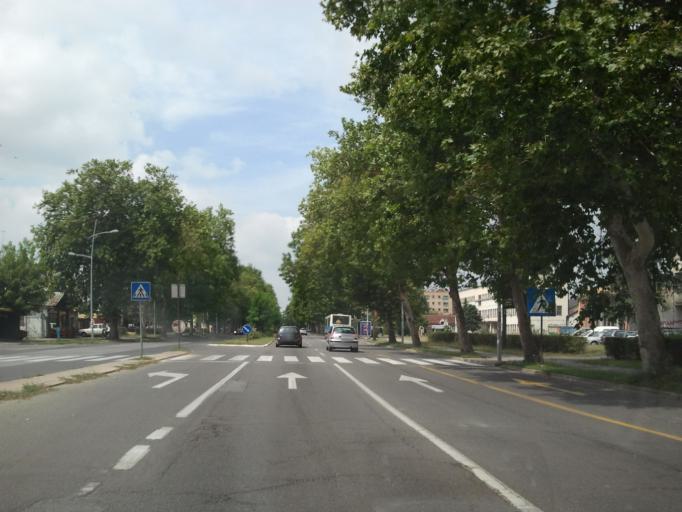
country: RS
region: Autonomna Pokrajina Vojvodina
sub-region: Juznobacki Okrug
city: Novi Sad
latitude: 45.2480
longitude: 19.8115
